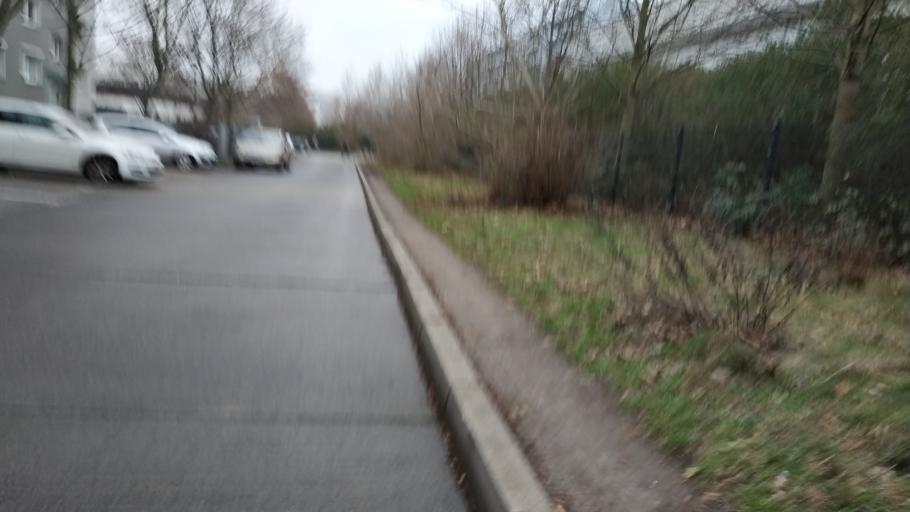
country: DE
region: Berlin
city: Marzahn
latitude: 52.5417
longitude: 13.5888
